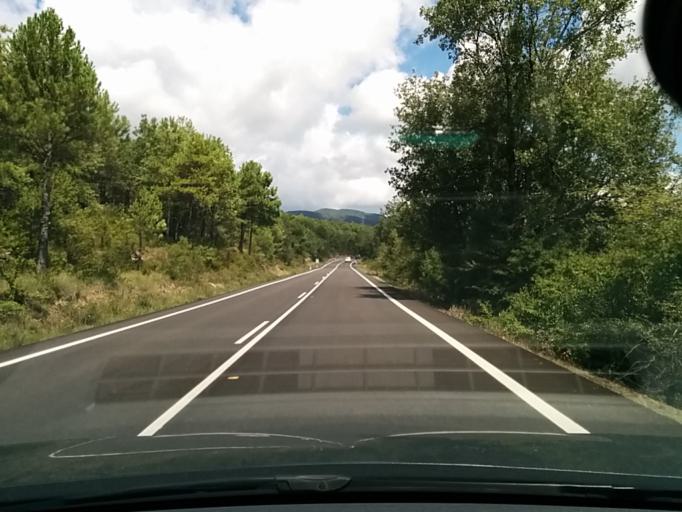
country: ES
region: Aragon
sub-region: Provincia de Huesca
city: Labuerda
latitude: 42.4391
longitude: 0.1305
